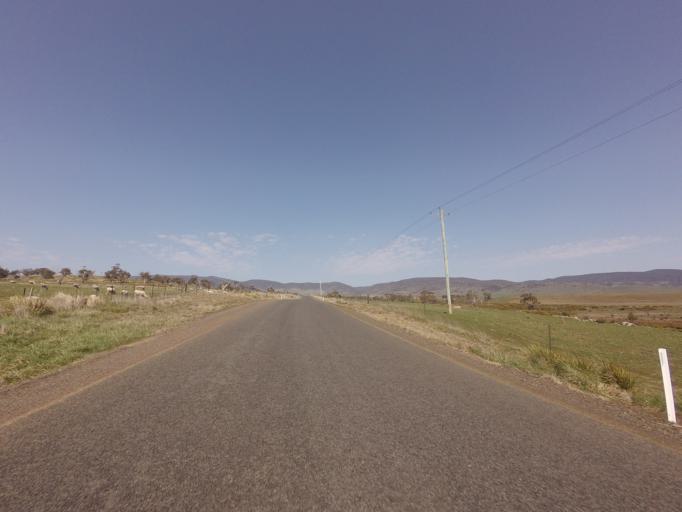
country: AU
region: Tasmania
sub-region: Northern Midlands
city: Evandale
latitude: -41.8059
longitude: 147.7528
